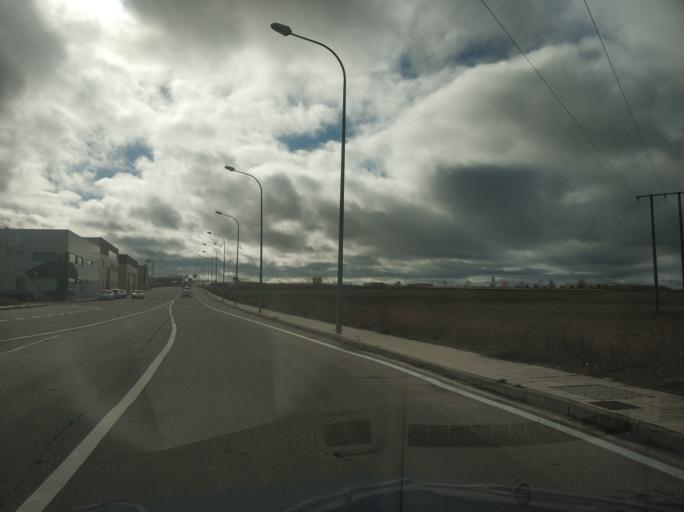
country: ES
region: Castille and Leon
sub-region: Provincia de Salamanca
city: Villares de la Reina
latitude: 40.9986
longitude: -5.6397
